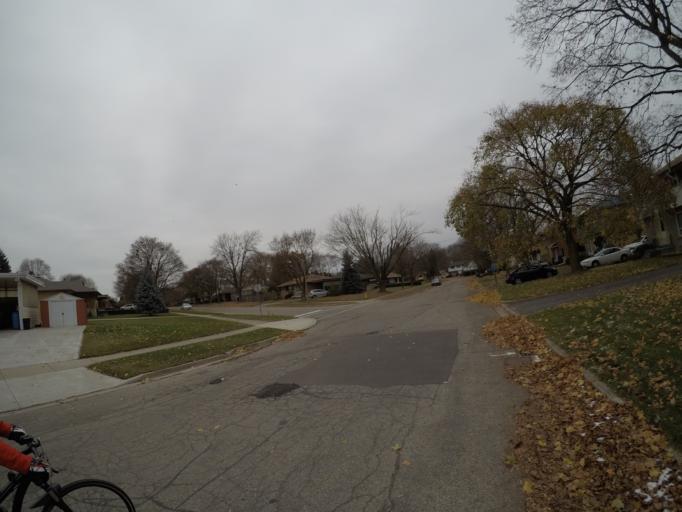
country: CA
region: Ontario
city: Waterloo
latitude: 43.4728
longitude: -80.5142
